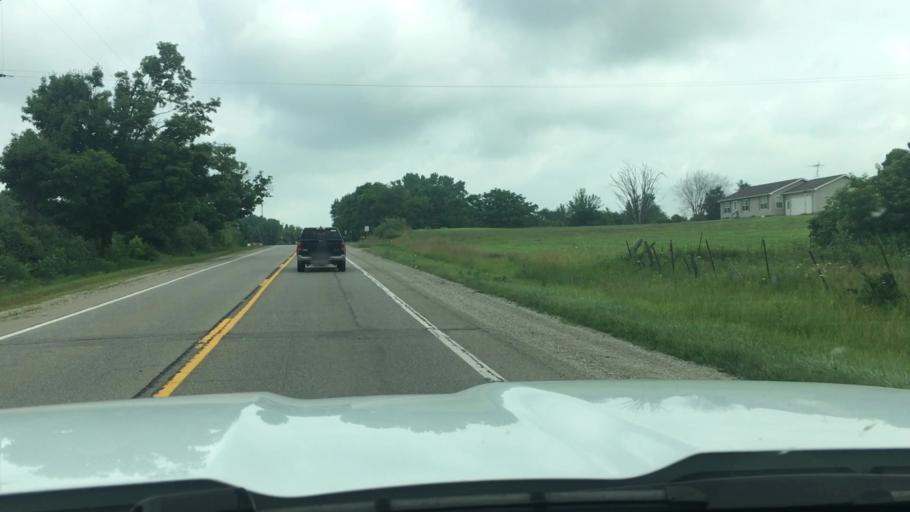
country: US
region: Michigan
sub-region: Lapeer County
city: Imlay City
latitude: 43.0713
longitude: -83.0750
